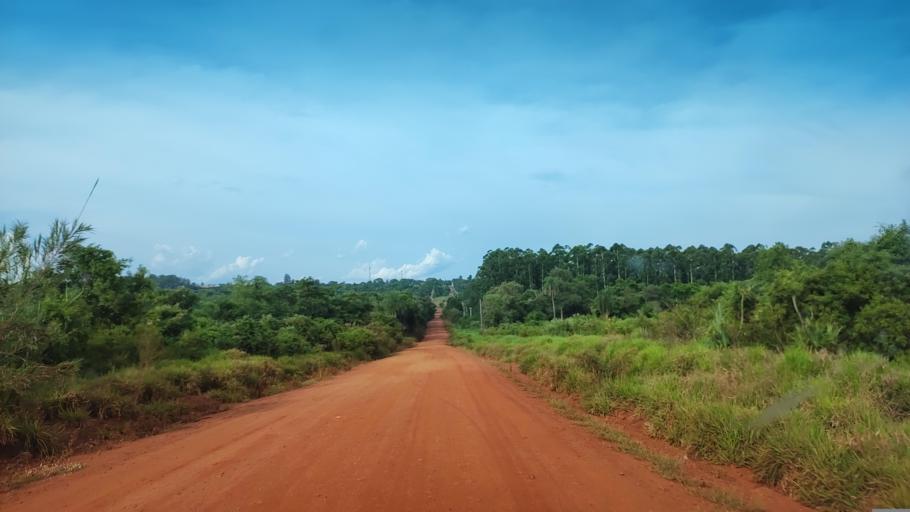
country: AR
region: Misiones
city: Gobernador Roca
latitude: -27.1415
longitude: -55.5240
